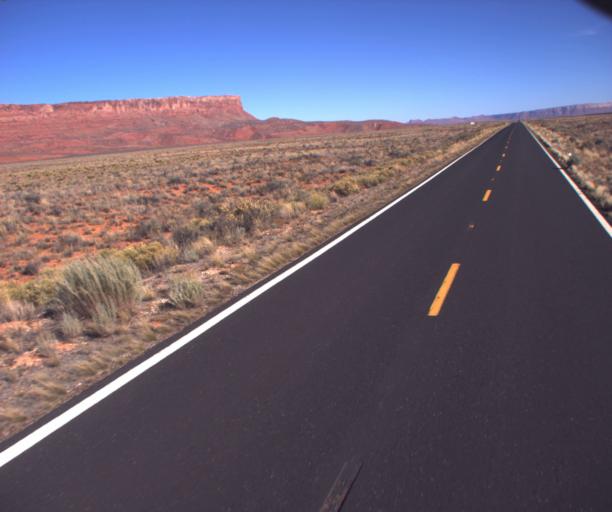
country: US
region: Arizona
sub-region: Coconino County
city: Page
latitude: 36.6997
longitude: -111.9247
